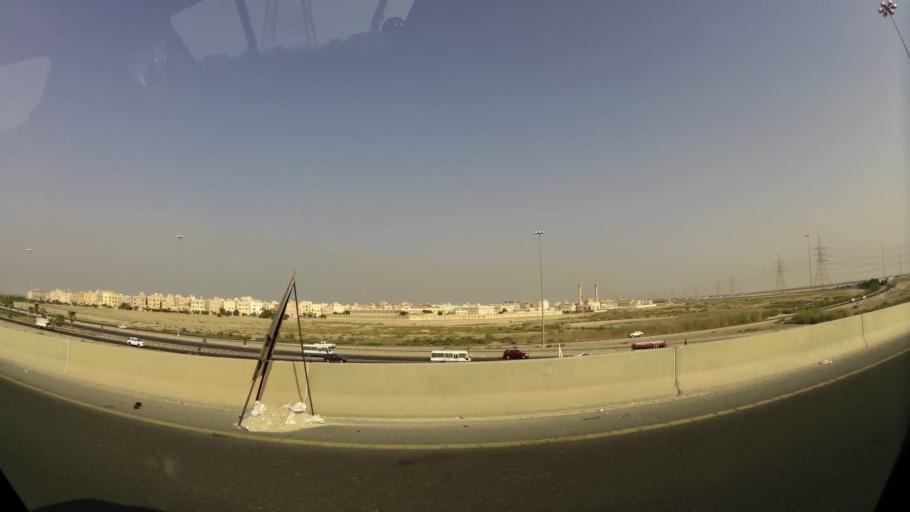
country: KW
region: Muhafazat al Jahra'
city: Al Jahra'
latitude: 29.3004
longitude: 47.7840
